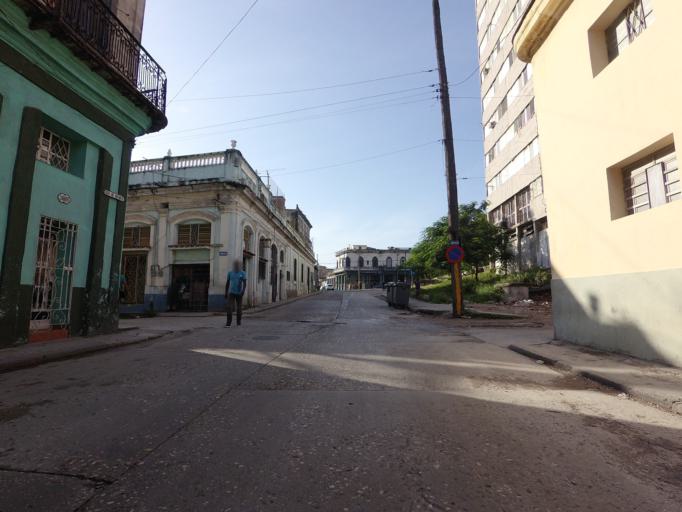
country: CU
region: La Habana
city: Cerro
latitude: 23.1183
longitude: -82.3711
